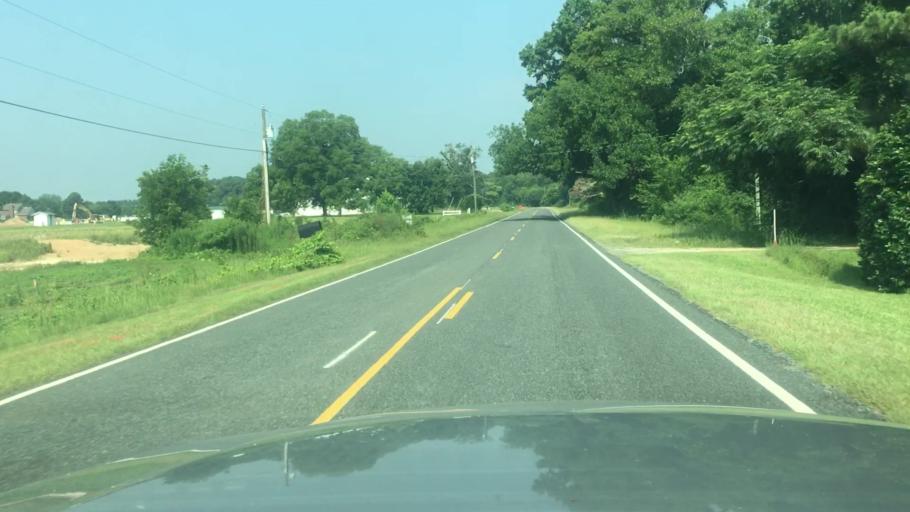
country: US
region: North Carolina
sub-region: Cumberland County
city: Hope Mills
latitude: 34.9091
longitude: -78.8649
